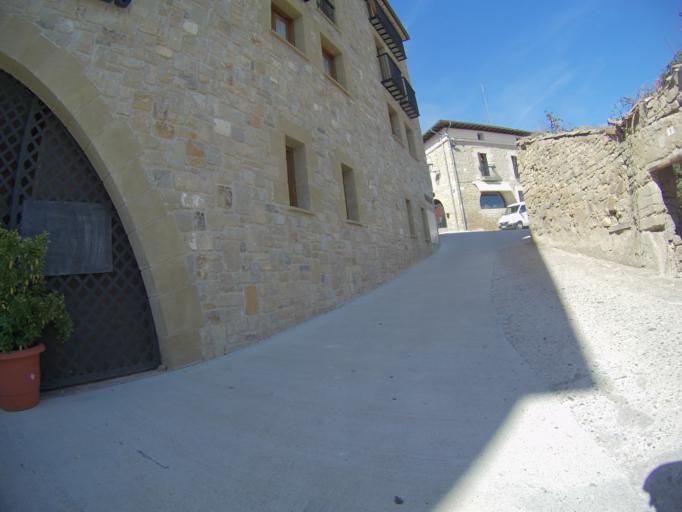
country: ES
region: Navarre
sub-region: Provincia de Navarra
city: Torres del Rio
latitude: 42.5515
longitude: -2.2708
